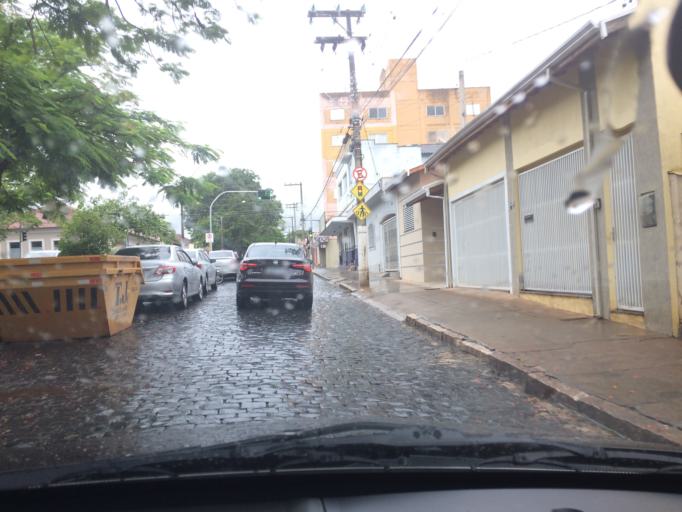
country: BR
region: Sao Paulo
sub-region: Casa Branca
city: Casa Branca
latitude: -21.7743
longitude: -47.0872
